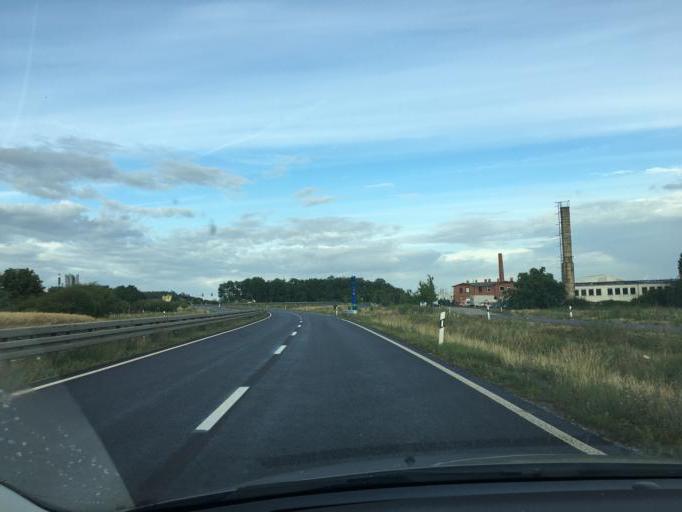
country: DE
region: Saxony-Anhalt
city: Bernburg
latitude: 51.8080
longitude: 11.7277
